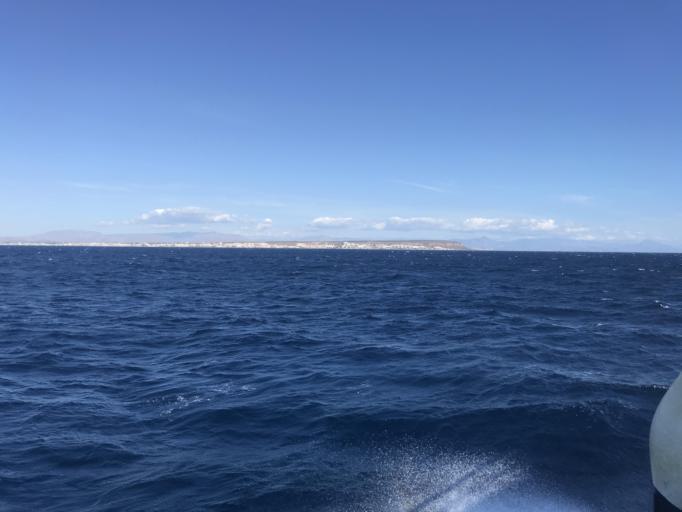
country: ES
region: Valencia
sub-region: Provincia de Alicante
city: Santa Pola
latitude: 38.1324
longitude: -0.5342
